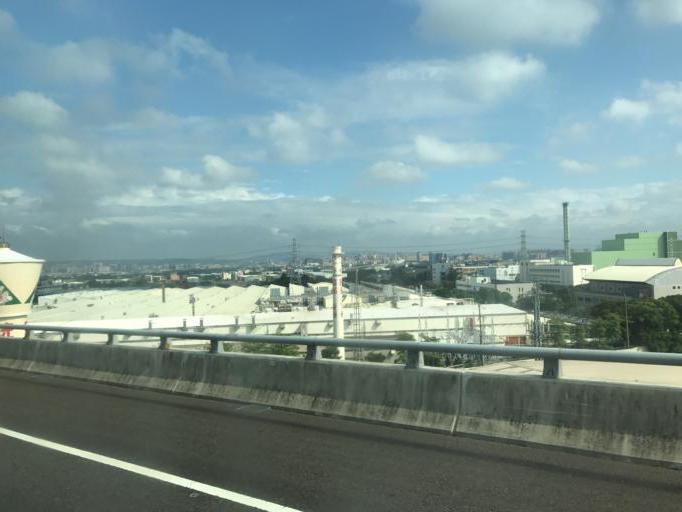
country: TW
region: Taiwan
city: Taoyuan City
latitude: 24.9949
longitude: 121.2442
